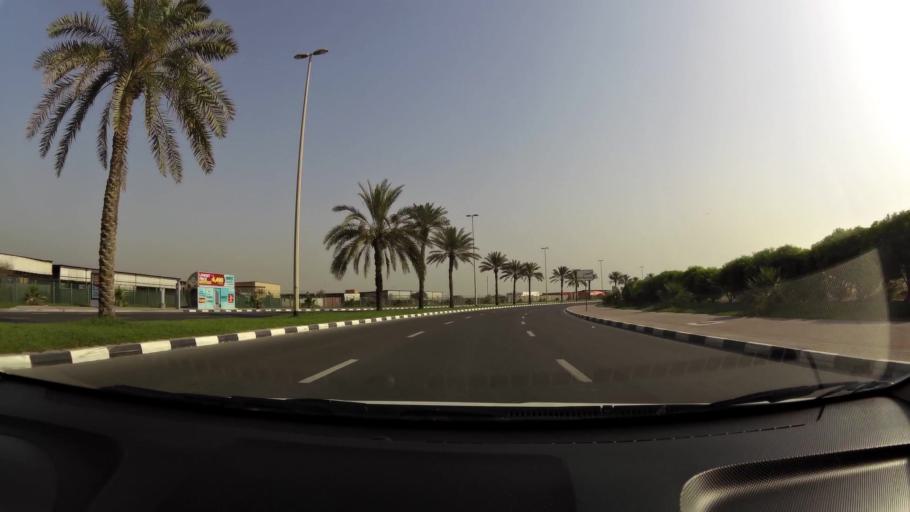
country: AE
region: Ash Shariqah
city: Sharjah
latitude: 25.3026
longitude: 55.3388
